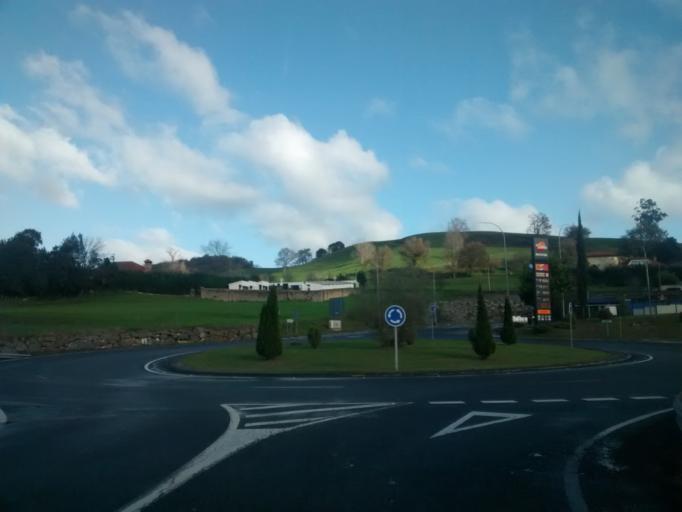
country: ES
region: Cantabria
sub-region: Provincia de Cantabria
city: Entrambasaguas
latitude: 43.3893
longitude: -3.6837
